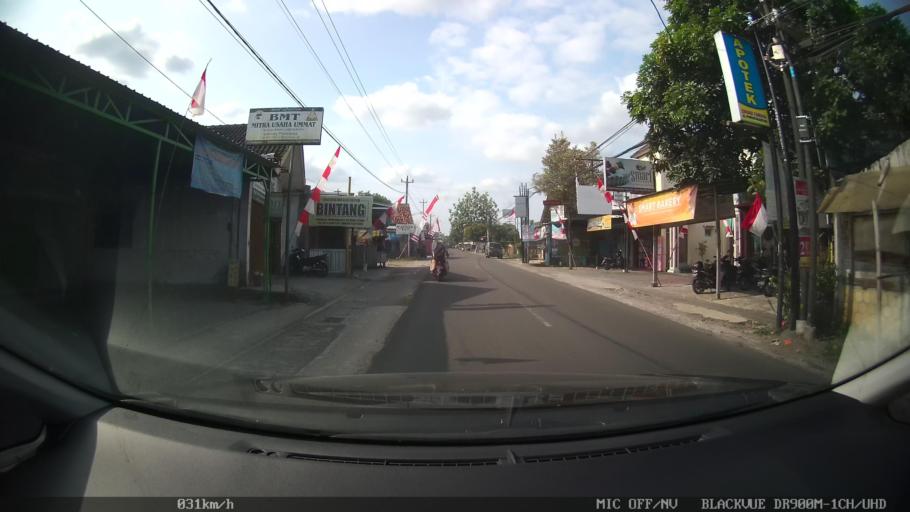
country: ID
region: Daerah Istimewa Yogyakarta
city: Depok
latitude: -7.7436
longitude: 110.4506
